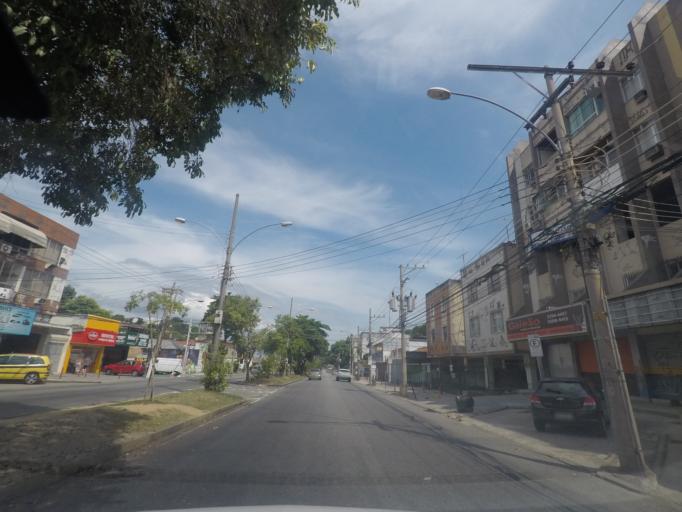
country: BR
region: Rio de Janeiro
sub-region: Rio De Janeiro
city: Rio de Janeiro
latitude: -22.8123
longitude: -43.1916
